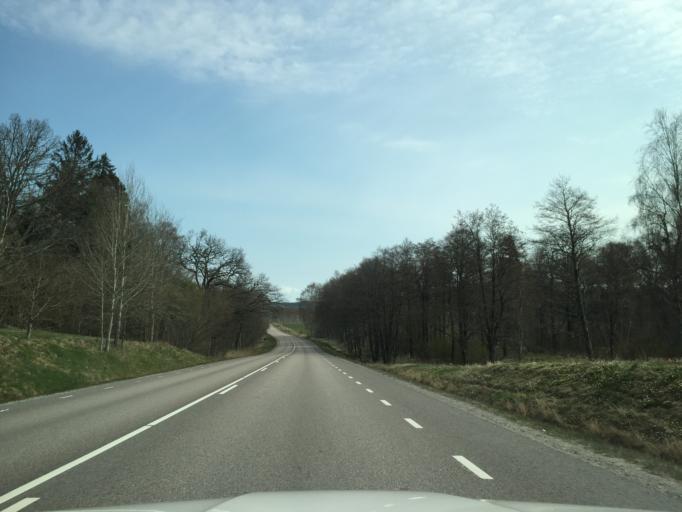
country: SE
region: Vaestra Goetaland
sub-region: Stenungsunds Kommun
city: Stora Hoga
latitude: 58.0671
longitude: 11.9290
